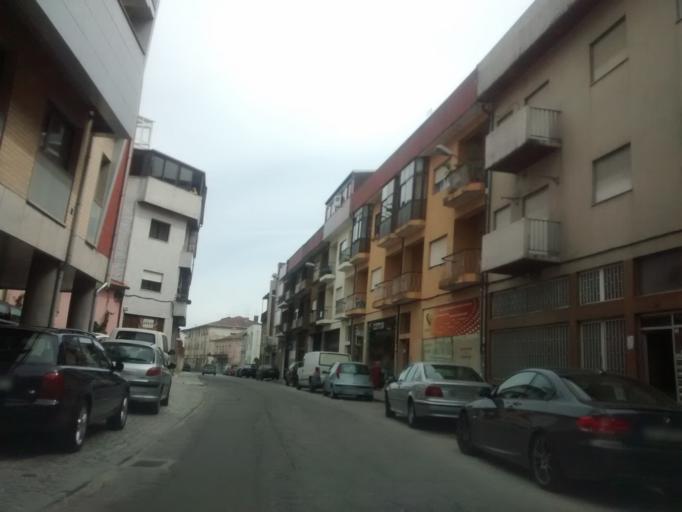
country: PT
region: Braga
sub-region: Braga
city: Braga
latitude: 41.5551
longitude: -8.4038
